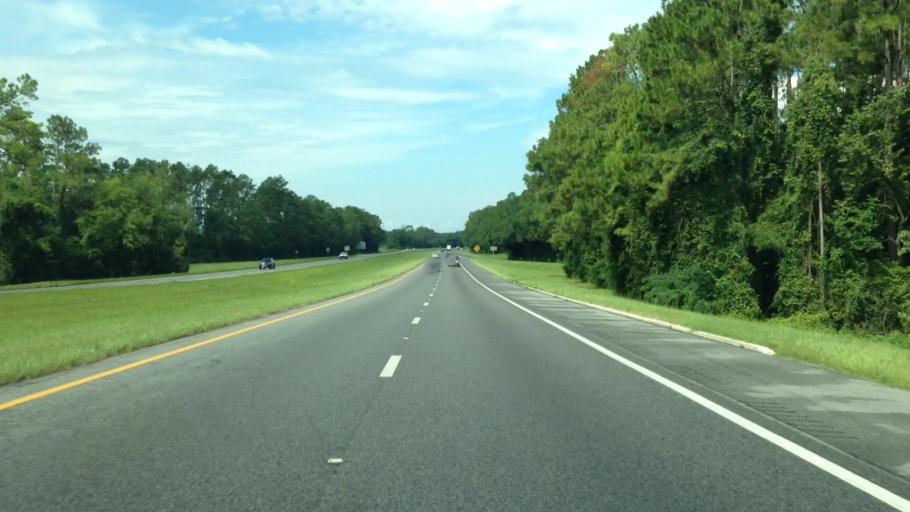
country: US
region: Florida
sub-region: Suwannee County
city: Live Oak
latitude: 30.3426
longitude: -83.0922
